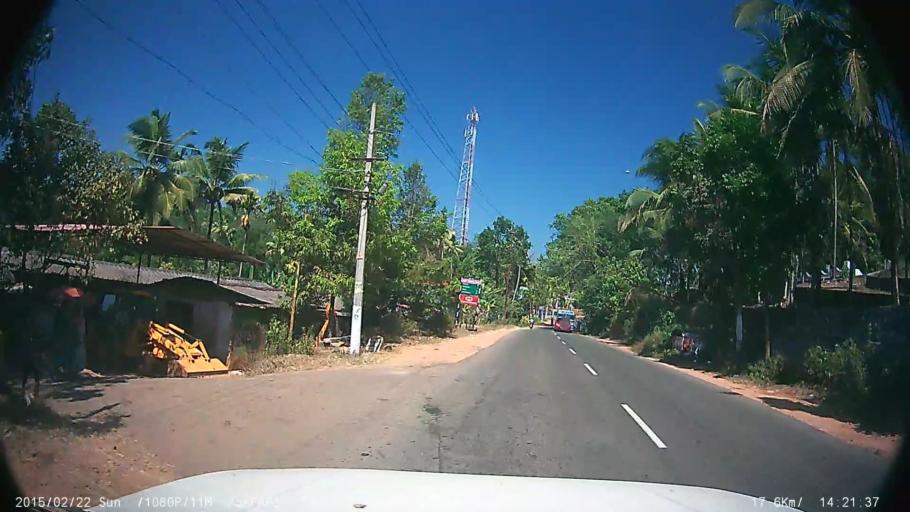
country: IN
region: Kerala
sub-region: Kottayam
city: Lalam
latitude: 9.5653
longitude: 76.7008
